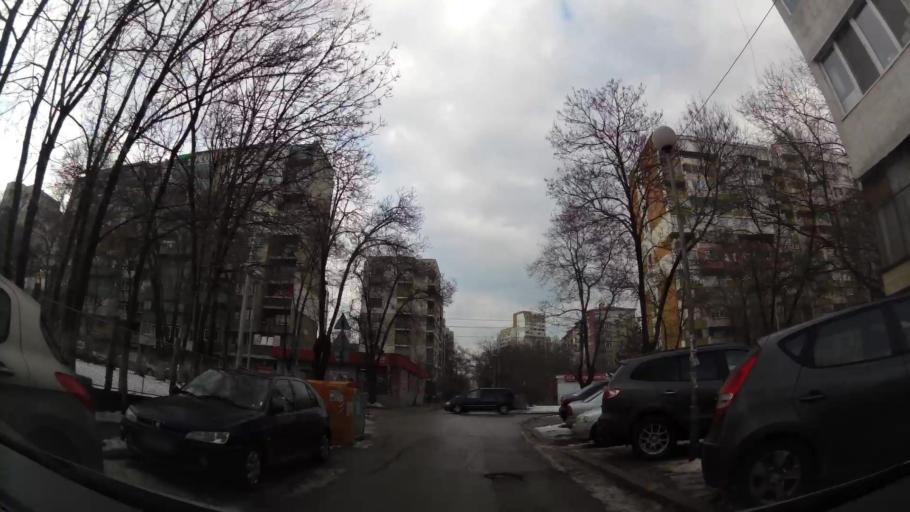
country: BG
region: Sofia-Capital
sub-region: Stolichna Obshtina
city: Sofia
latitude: 42.7076
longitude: 23.2897
